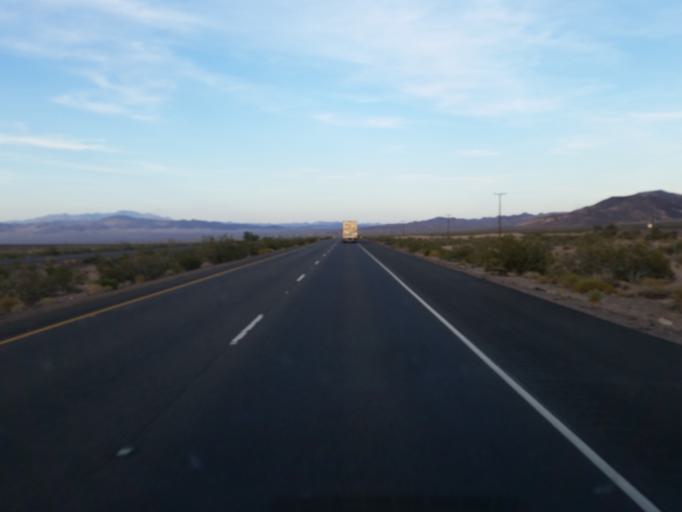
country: US
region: California
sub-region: San Bernardino County
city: Joshua Tree
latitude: 34.7278
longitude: -116.2554
